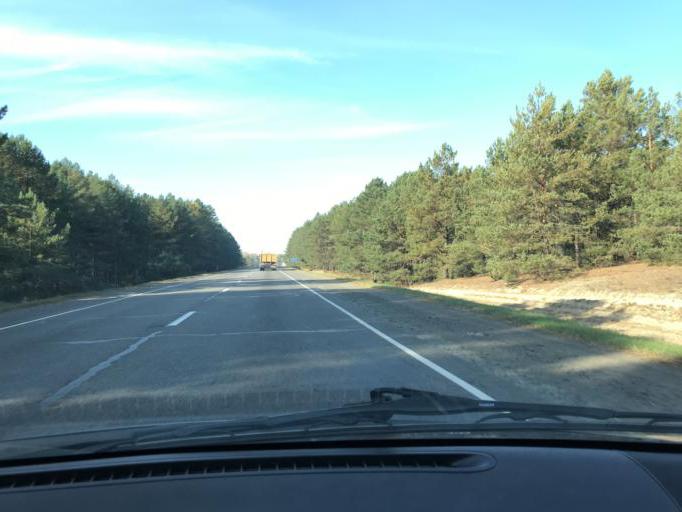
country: BY
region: Brest
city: Davyd-Haradok
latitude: 52.2469
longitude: 27.1014
